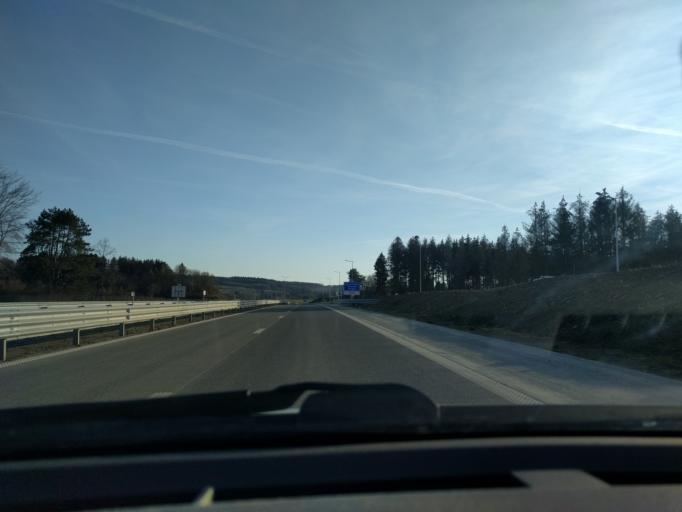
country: BE
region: Wallonia
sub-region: Province de Namur
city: Couvin
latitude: 50.0613
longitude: 4.5053
